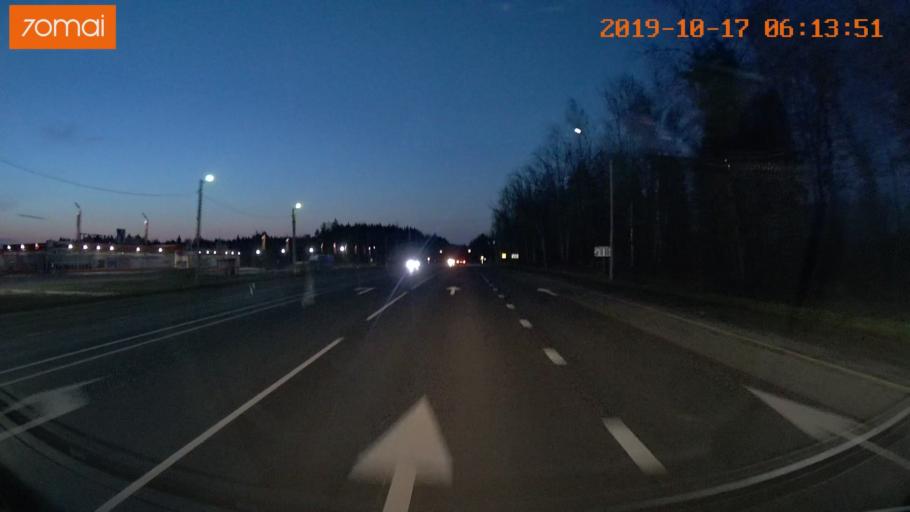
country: RU
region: Ivanovo
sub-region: Gorod Ivanovo
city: Ivanovo
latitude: 56.8930
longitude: 40.9388
